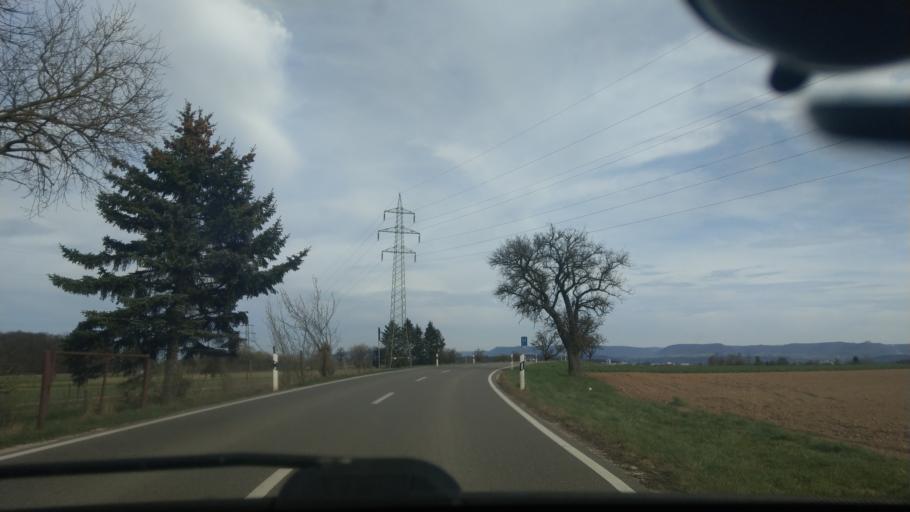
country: DE
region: Baden-Wuerttemberg
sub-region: Regierungsbezirk Stuttgart
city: Wolfschlugen
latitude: 48.6645
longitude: 9.2663
